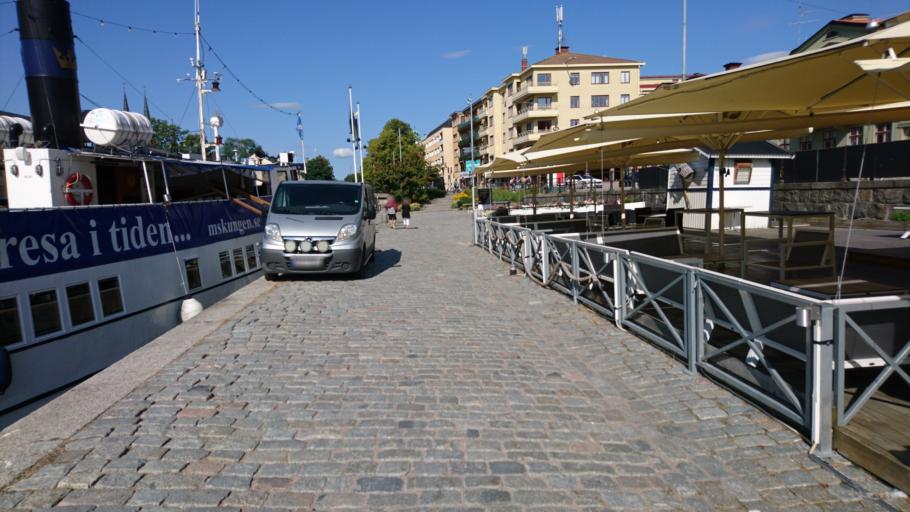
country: SE
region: Uppsala
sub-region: Uppsala Kommun
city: Uppsala
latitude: 59.8545
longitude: 17.6424
